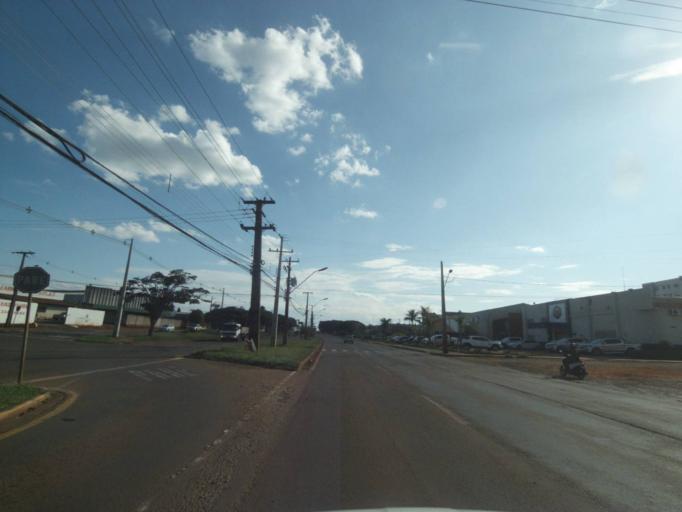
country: BR
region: Parana
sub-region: Londrina
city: Londrina
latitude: -23.3535
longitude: -51.1485
